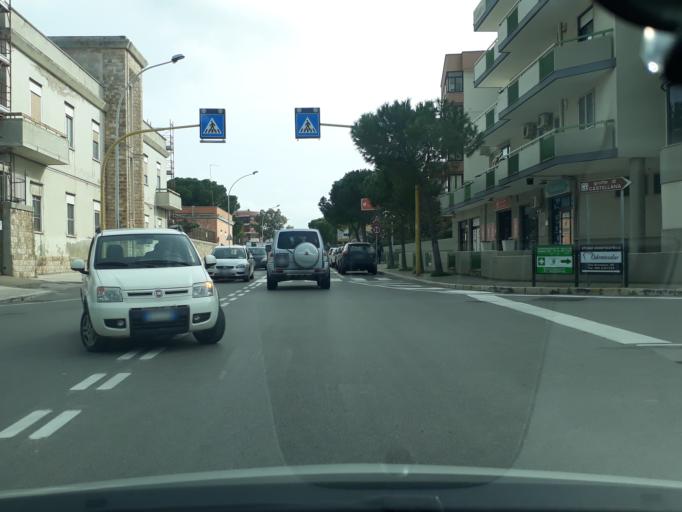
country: IT
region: Apulia
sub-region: Provincia di Bari
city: Monopoli
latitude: 40.9505
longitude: 17.2880
